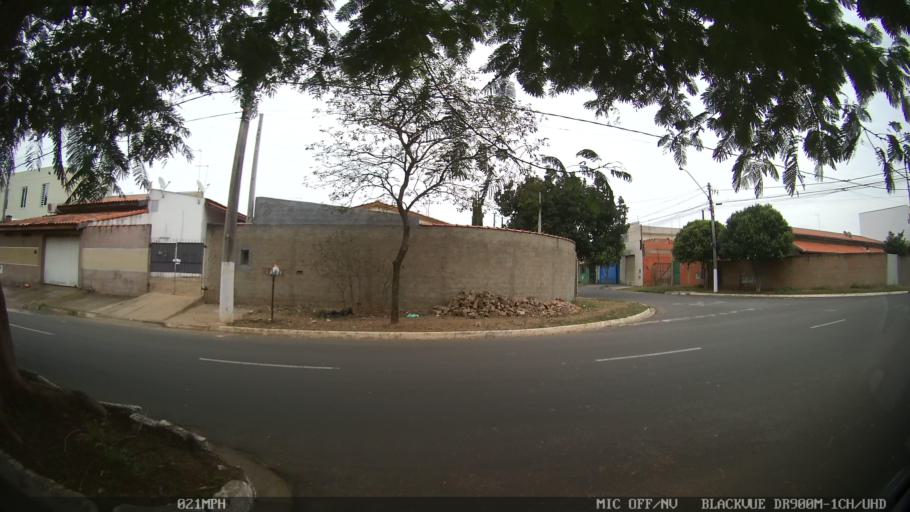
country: BR
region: Sao Paulo
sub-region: Paulinia
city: Paulinia
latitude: -22.7169
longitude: -47.1673
